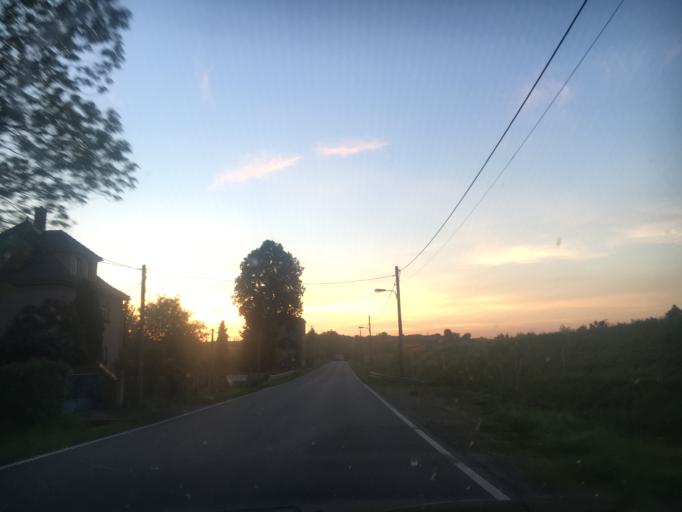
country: DE
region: Thuringia
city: Crimla
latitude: 50.8272
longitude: 12.0749
